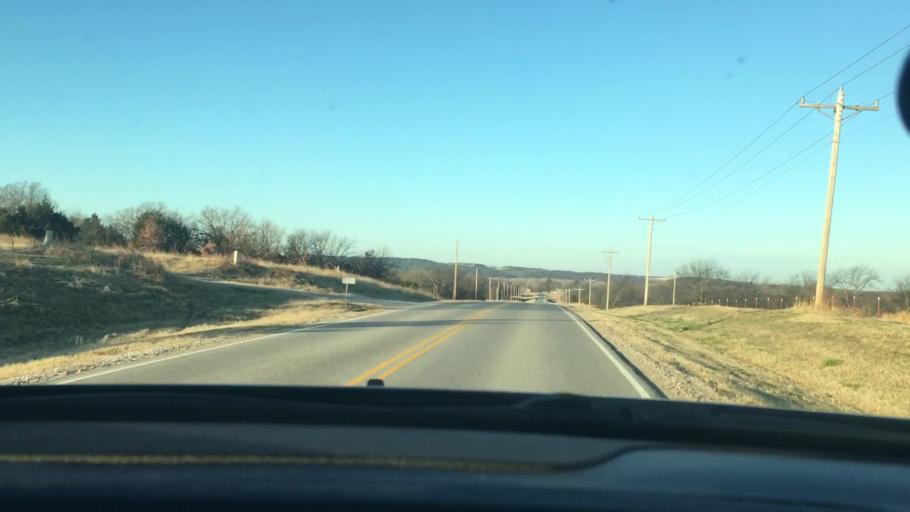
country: US
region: Oklahoma
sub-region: Murray County
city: Davis
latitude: 34.4774
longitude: -97.1192
